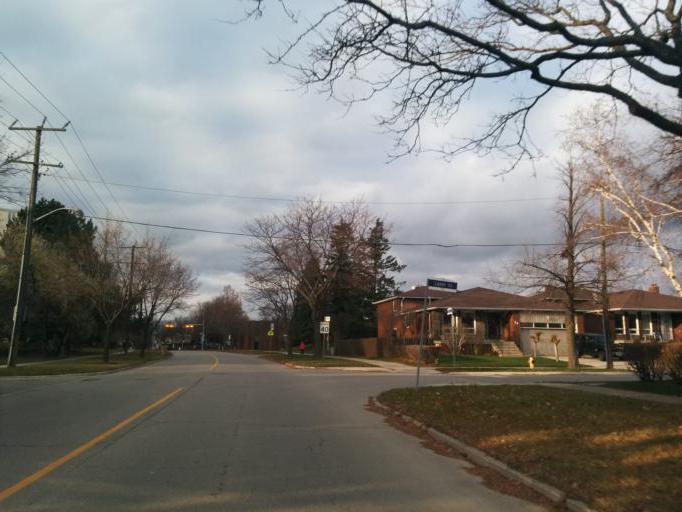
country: CA
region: Ontario
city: Etobicoke
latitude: 43.6427
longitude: -79.5864
